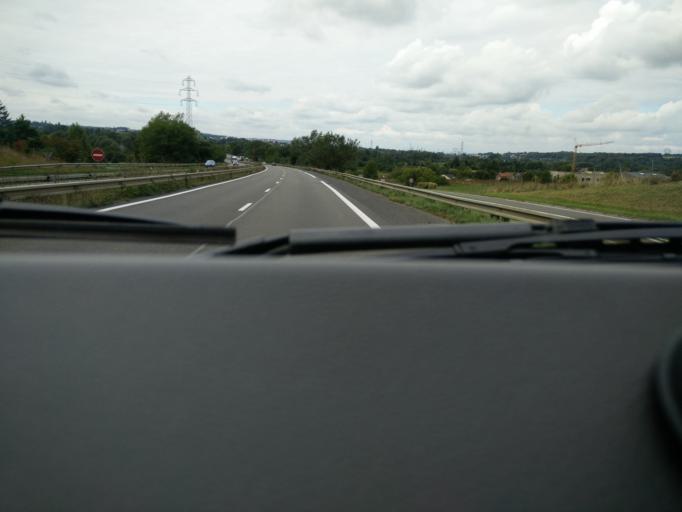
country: FR
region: Champagne-Ardenne
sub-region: Departement des Ardennes
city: Lumes
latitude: 49.7382
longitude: 4.7865
